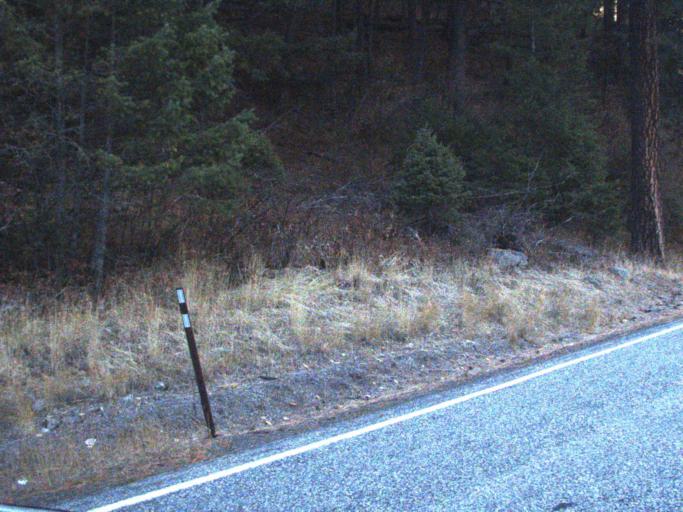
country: US
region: Washington
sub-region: Ferry County
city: Republic
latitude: 48.5504
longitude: -118.7477
